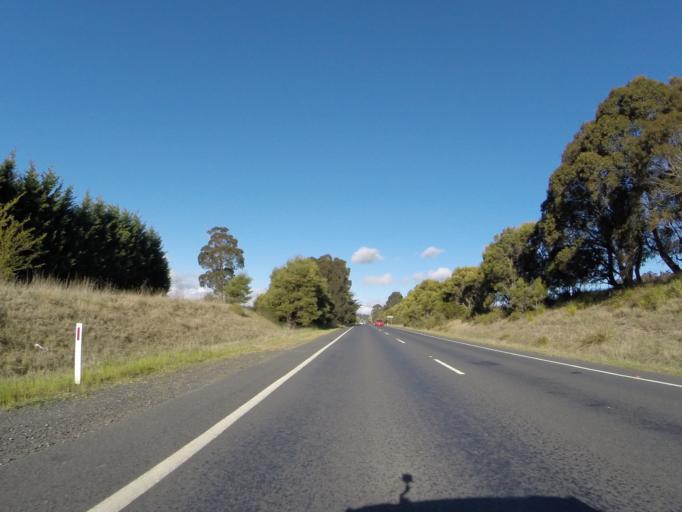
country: AU
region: New South Wales
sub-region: Wingecarribee
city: Moss Vale
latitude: -34.5722
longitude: 150.4586
